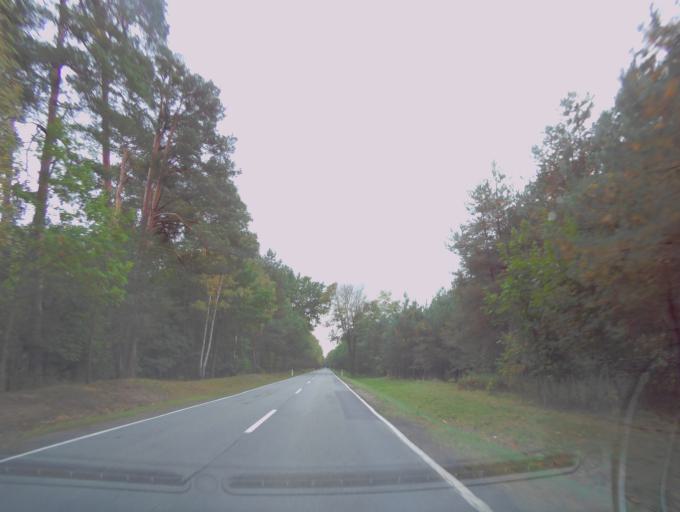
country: PL
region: Subcarpathian Voivodeship
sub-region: Powiat nizanski
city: Krzeszow
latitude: 50.3805
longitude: 22.3100
